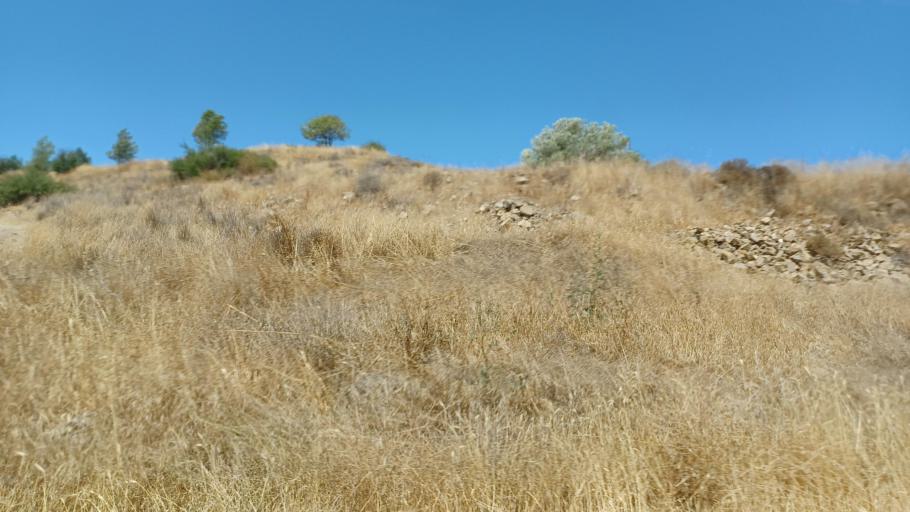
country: CY
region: Larnaka
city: Troulloi
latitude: 35.0328
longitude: 33.6378
